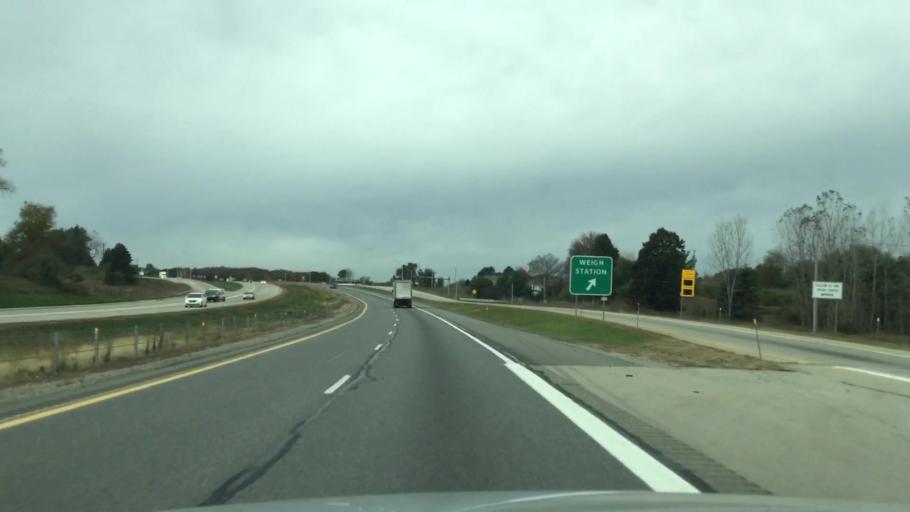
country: US
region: Michigan
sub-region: Jackson County
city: Grass Lake
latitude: 42.2935
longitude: -84.1713
